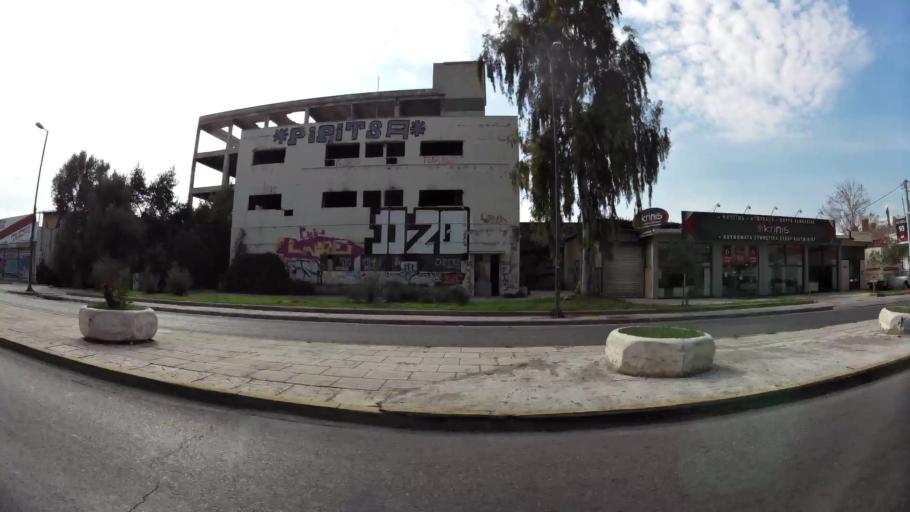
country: GR
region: Attica
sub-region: Nomarchia Athinas
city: Aigaleo
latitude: 37.9858
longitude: 23.6995
